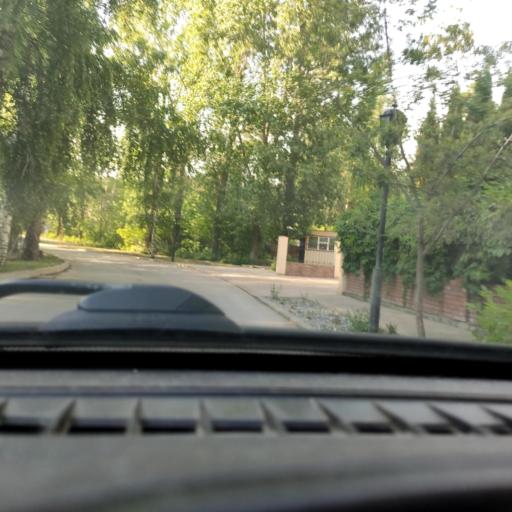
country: RU
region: Samara
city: Tol'yatti
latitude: 53.4751
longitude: 49.3279
